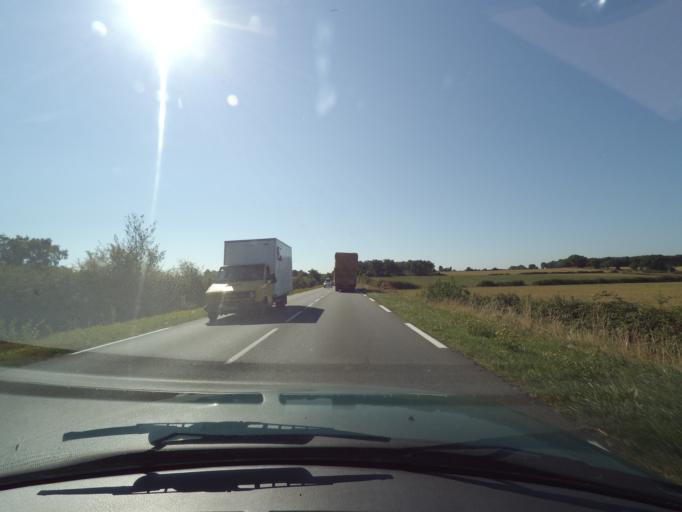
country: FR
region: Poitou-Charentes
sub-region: Departement de la Vienne
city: Lussac-les-Chateaux
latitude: 46.3920
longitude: 0.7372
